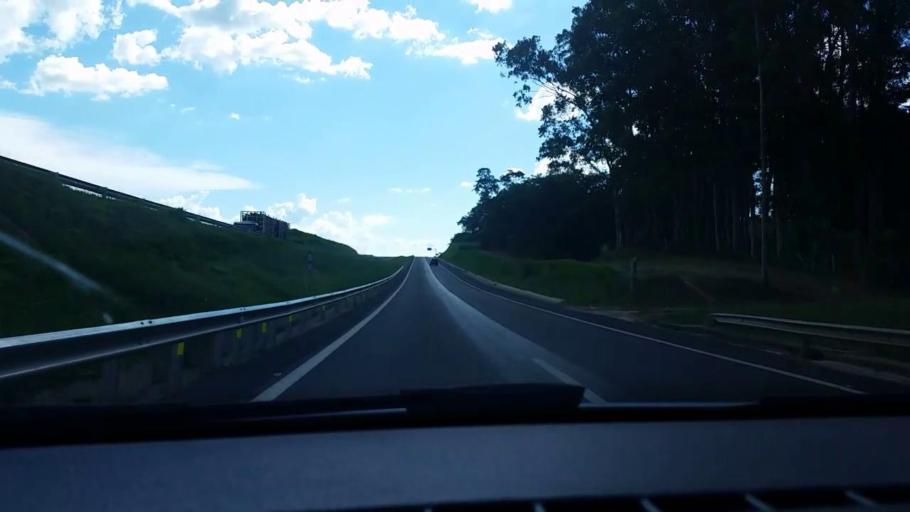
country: BR
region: Sao Paulo
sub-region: Bauru
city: Bauru
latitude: -22.4442
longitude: -49.1551
